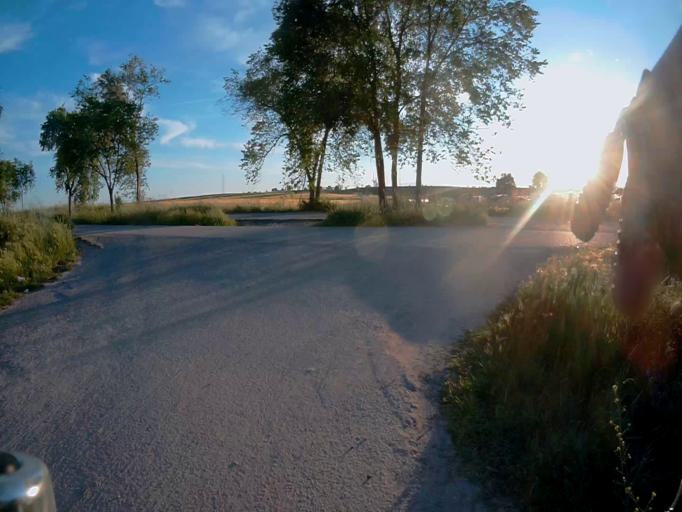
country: ES
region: Madrid
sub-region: Provincia de Madrid
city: Alcorcon
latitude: 40.3309
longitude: -3.8081
